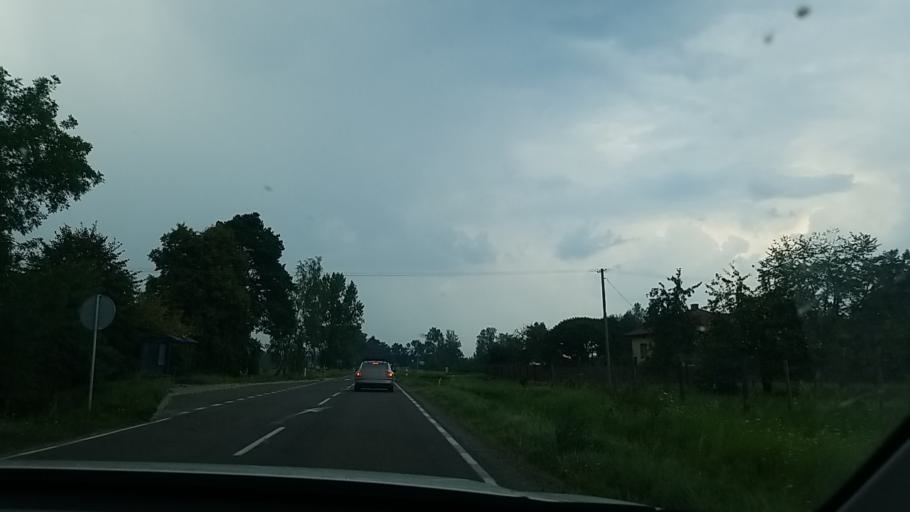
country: PL
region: Lublin Voivodeship
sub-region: Powiat leczynski
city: Cycow
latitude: 51.2728
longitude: 23.0965
